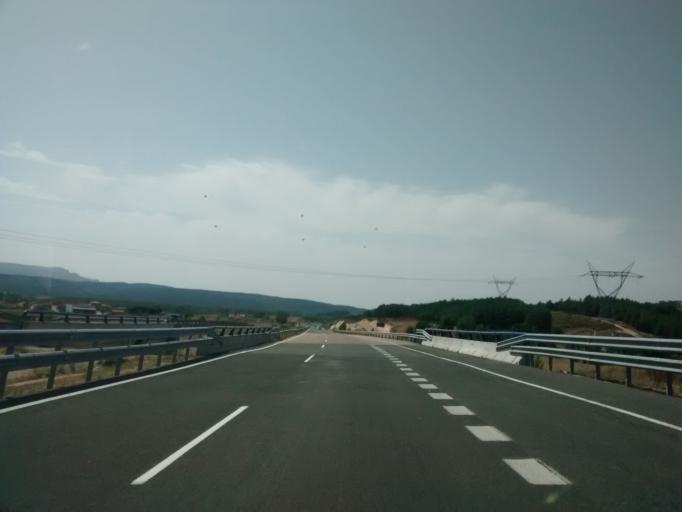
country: ES
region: Castille and Leon
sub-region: Provincia de Palencia
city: Aguilar de Campoo
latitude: 42.7499
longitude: -4.2932
